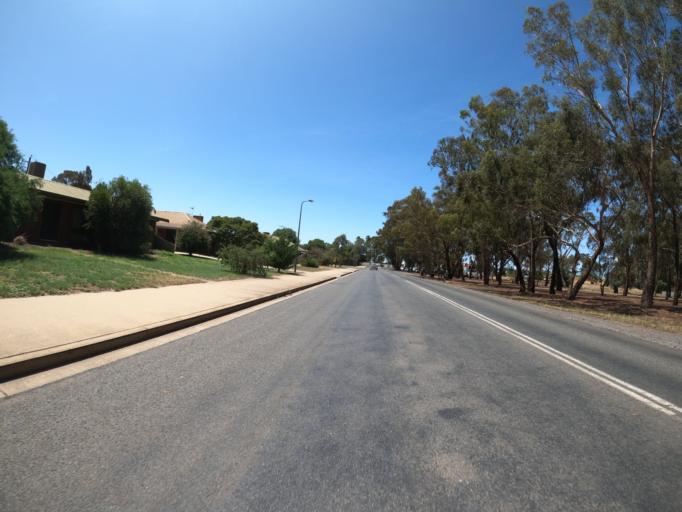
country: AU
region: New South Wales
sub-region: Corowa Shire
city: Mulwala
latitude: -36.0019
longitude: 145.9999
